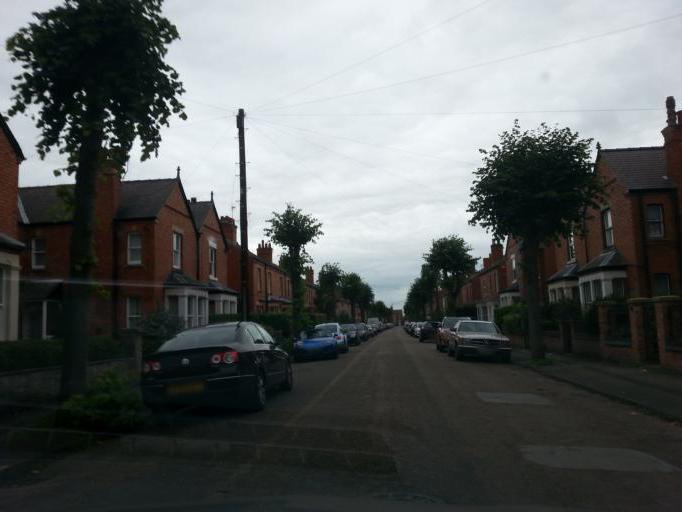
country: GB
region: England
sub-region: Nottinghamshire
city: Newark on Trent
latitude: 53.0704
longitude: -0.7987
